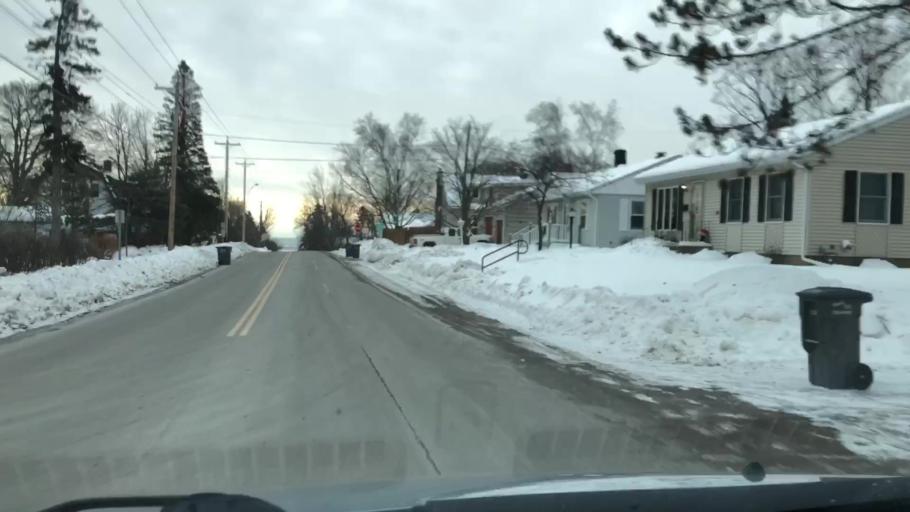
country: US
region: Minnesota
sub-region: Saint Louis County
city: Arnold
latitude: 46.8349
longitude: -92.0638
